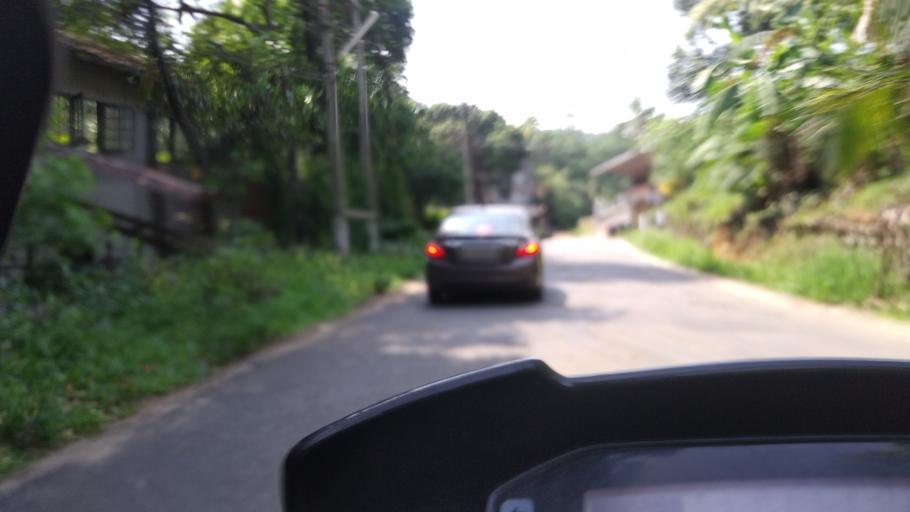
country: IN
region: Kerala
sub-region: Kottayam
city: Erattupetta
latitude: 9.6988
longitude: 76.8141
